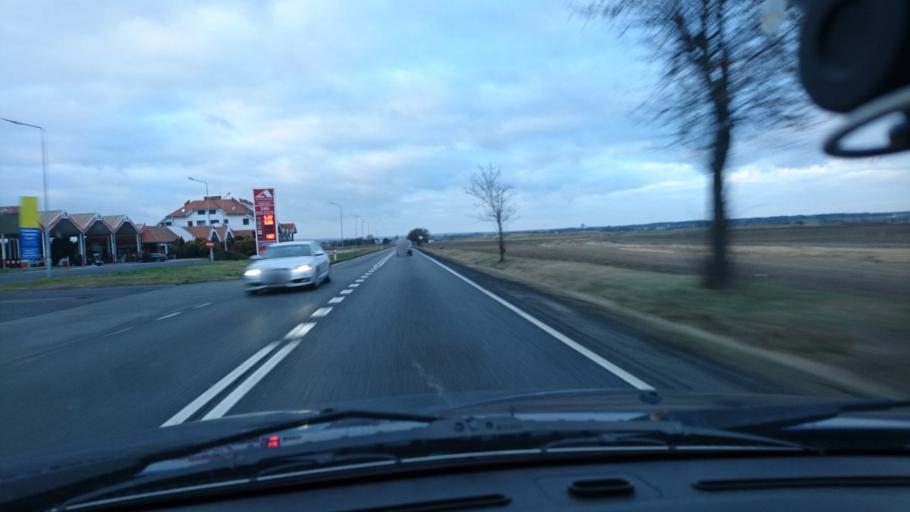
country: PL
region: Greater Poland Voivodeship
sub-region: Powiat kepinski
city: Baranow
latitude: 51.2490
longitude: 18.0163
